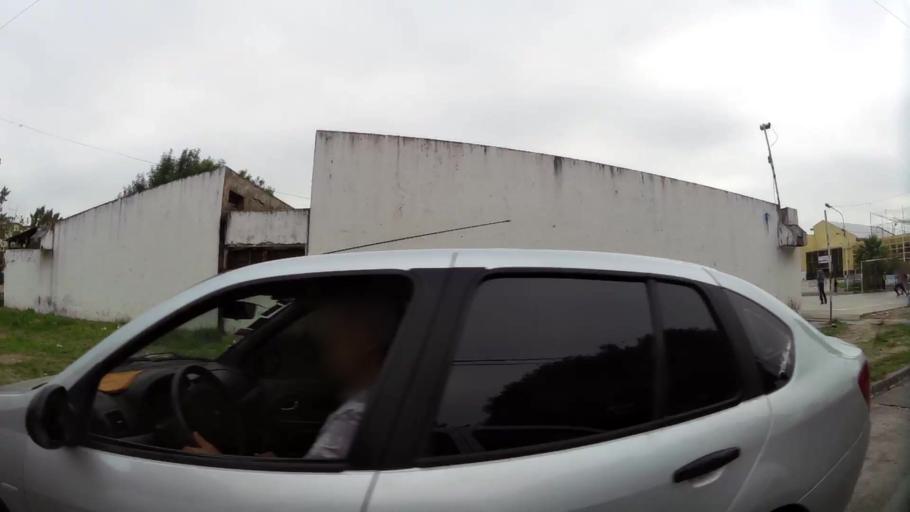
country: AR
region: Buenos Aires
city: San Justo
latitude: -34.6933
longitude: -58.5766
